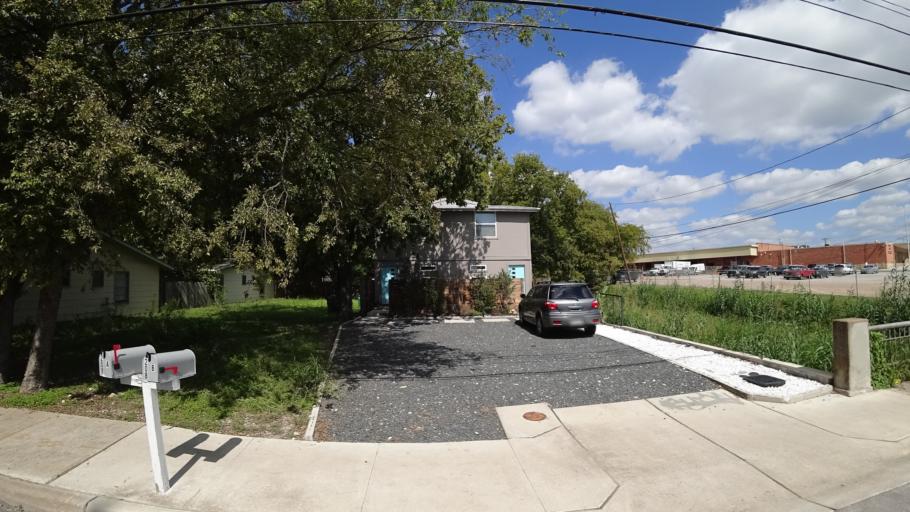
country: US
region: Texas
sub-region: Travis County
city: Austin
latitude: 30.3278
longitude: -97.7181
